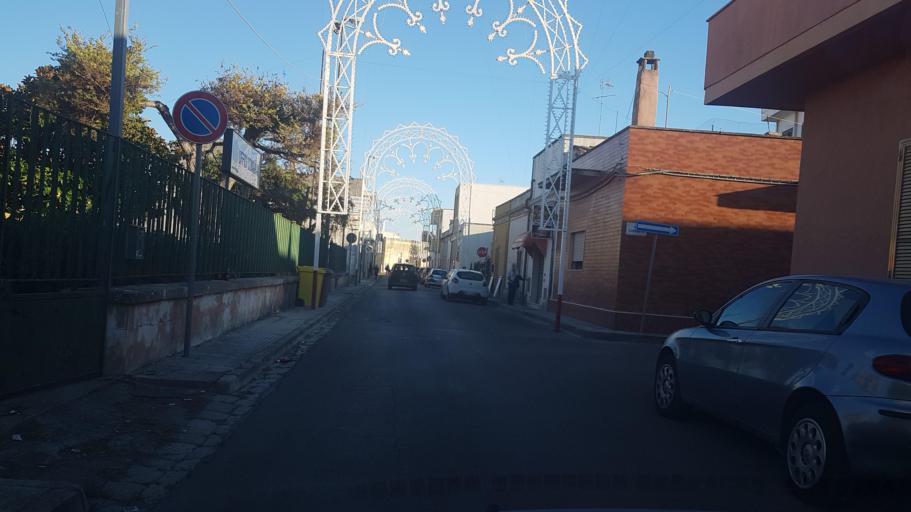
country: IT
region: Apulia
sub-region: Provincia di Lecce
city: Struda
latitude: 40.3193
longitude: 18.2823
